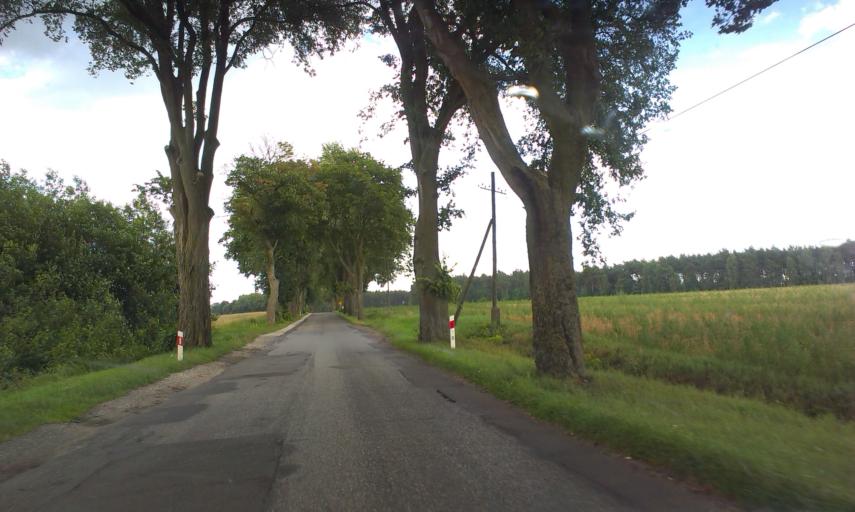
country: PL
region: Greater Poland Voivodeship
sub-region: Powiat zlotowski
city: Krajenka
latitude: 53.2879
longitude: 16.9977
